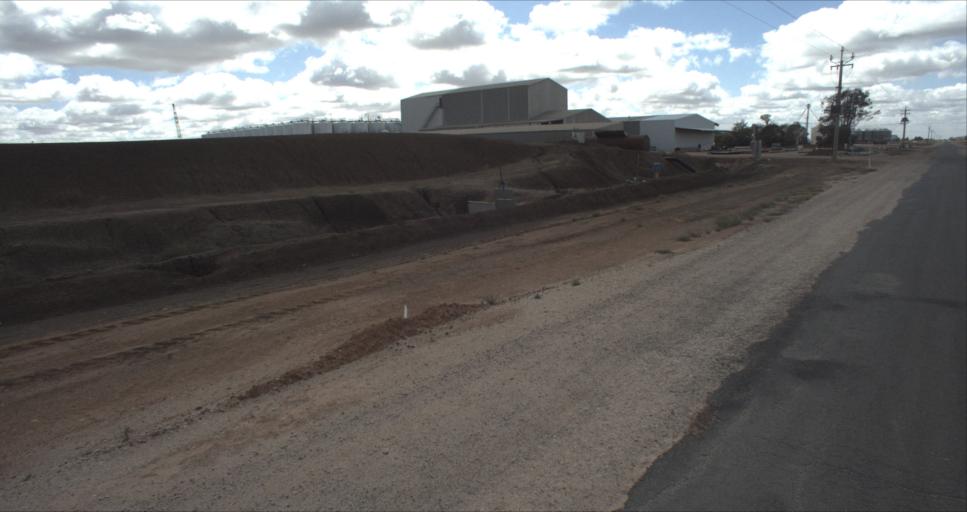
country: AU
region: New South Wales
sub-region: Murrumbidgee Shire
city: Darlington Point
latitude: -34.5756
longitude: 146.1748
